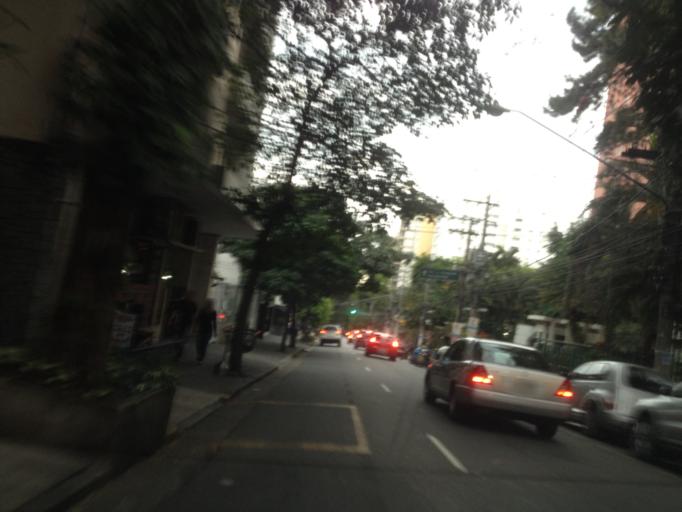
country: BR
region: Sao Paulo
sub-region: Sao Paulo
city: Sao Paulo
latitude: -23.5603
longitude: -46.6680
